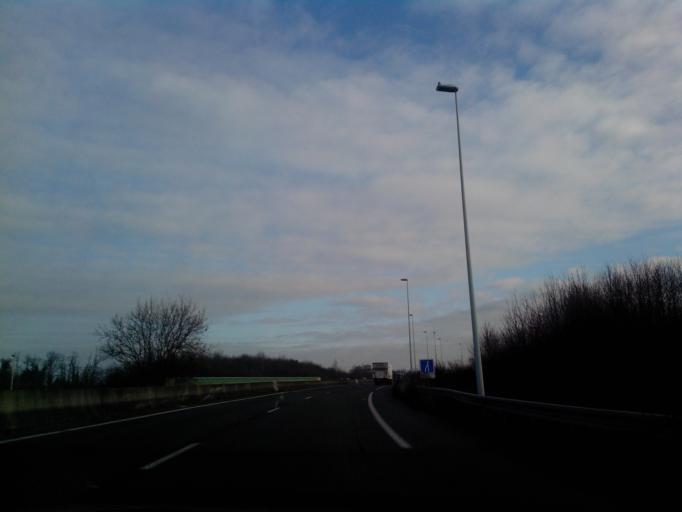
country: FR
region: Ile-de-France
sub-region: Departement du Val-d'Oise
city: Mery-sur-Oise
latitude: 49.0505
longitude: 2.1847
